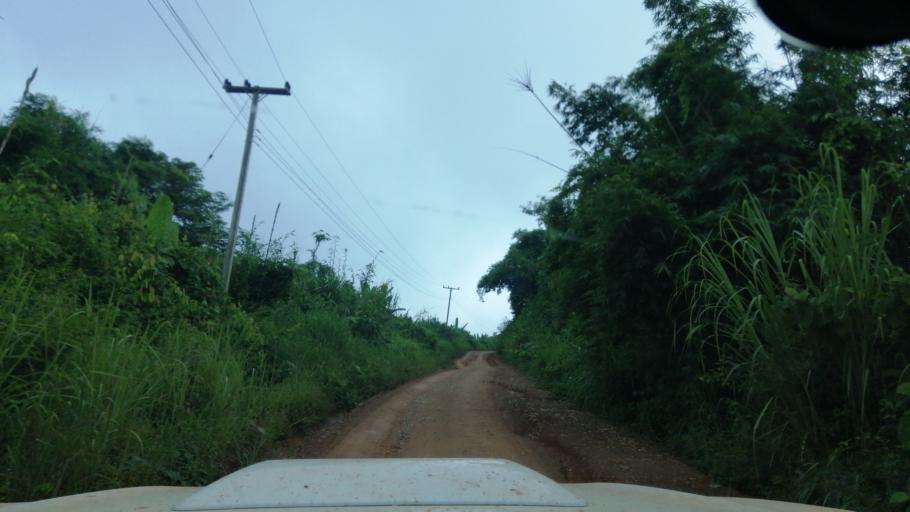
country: TH
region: Nan
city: Mae Charim
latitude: 18.5160
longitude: 101.5599
